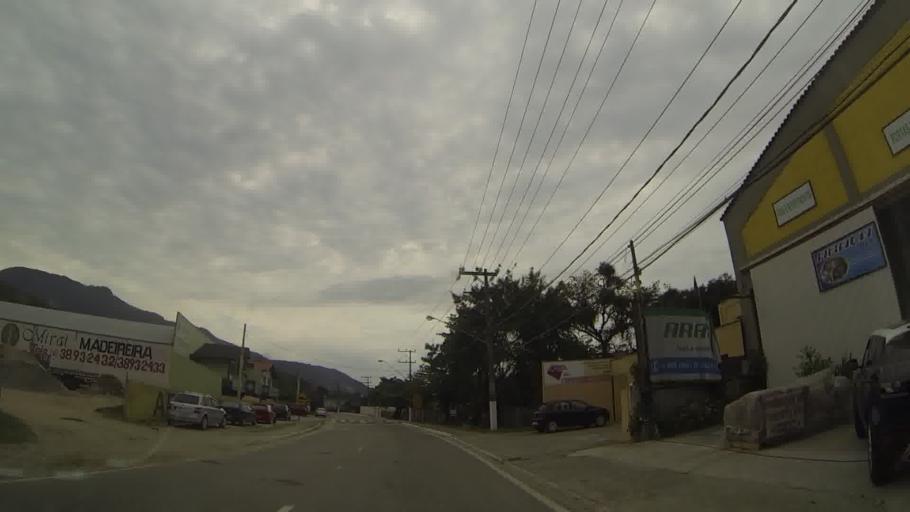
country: BR
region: Sao Paulo
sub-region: Sao Sebastiao
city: Sao Sebastiao
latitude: -23.8168
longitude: -45.4083
